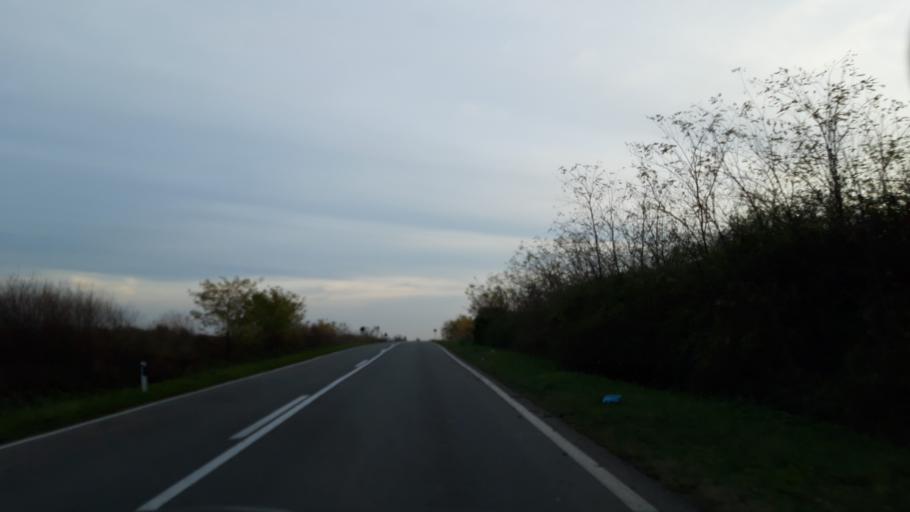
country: RS
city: Ostojicevo
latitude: 45.9040
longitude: 20.1548
